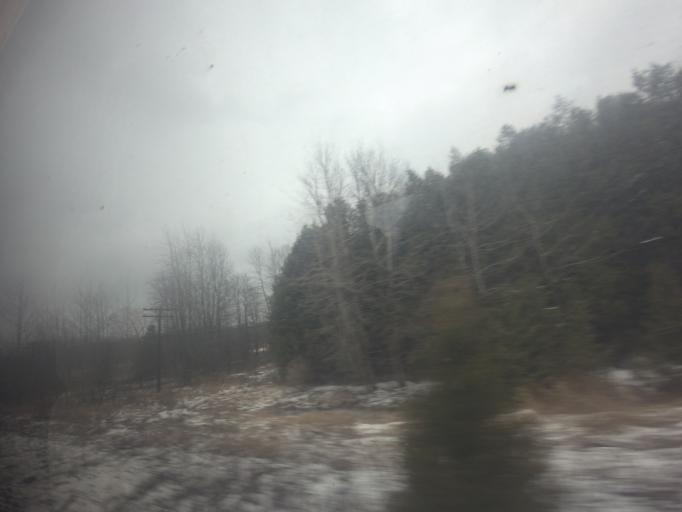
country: CA
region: Ontario
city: Cobourg
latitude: 43.9558
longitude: -78.2212
